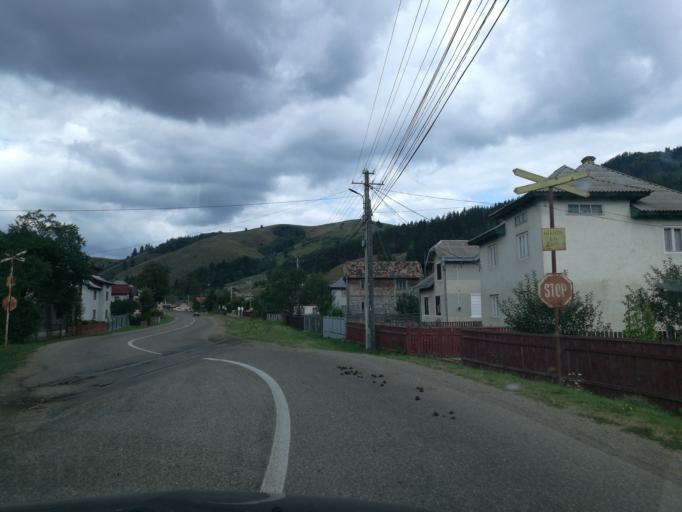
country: RO
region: Suceava
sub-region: Comuna Frumosu
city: Frumosu
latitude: 47.6146
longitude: 25.6415
